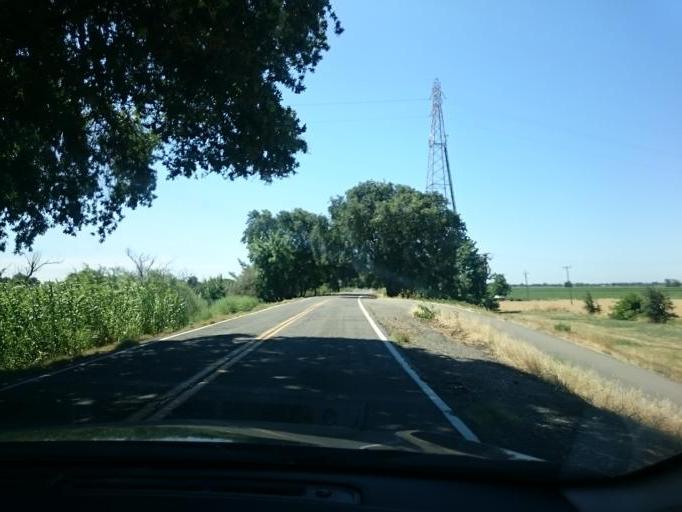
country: US
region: California
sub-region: Sacramento County
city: Parkway
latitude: 38.4679
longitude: -121.5058
